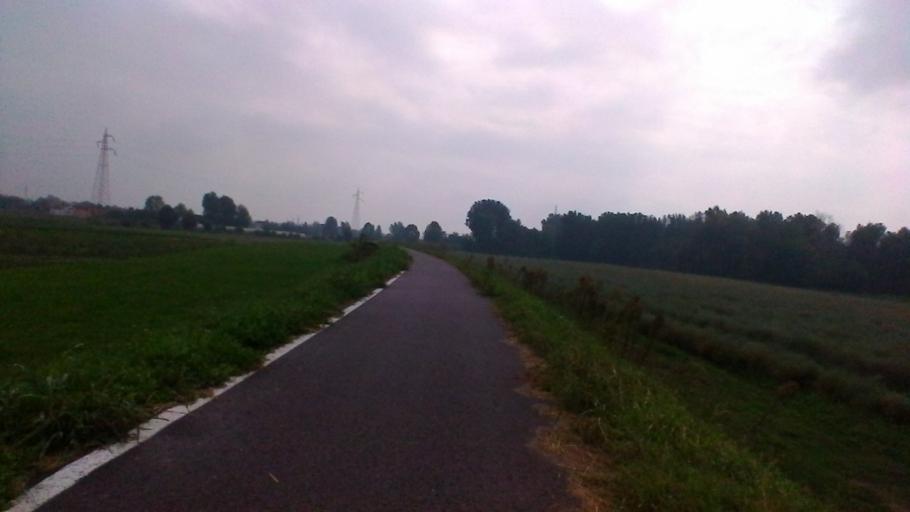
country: IT
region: Veneto
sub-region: Provincia di Verona
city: San Giovanni Lupatoto
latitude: 45.4097
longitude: 11.0264
